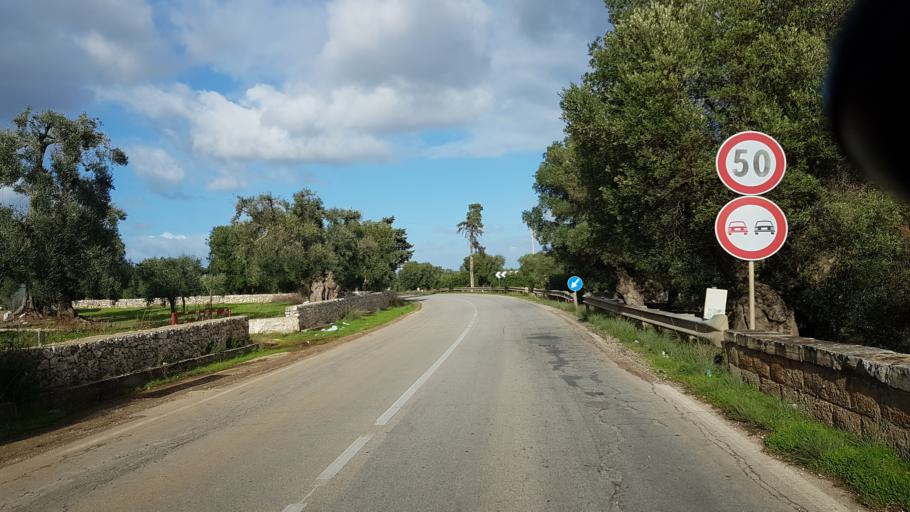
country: IT
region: Apulia
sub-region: Provincia di Brindisi
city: Ostuni
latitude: 40.7363
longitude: 17.5647
